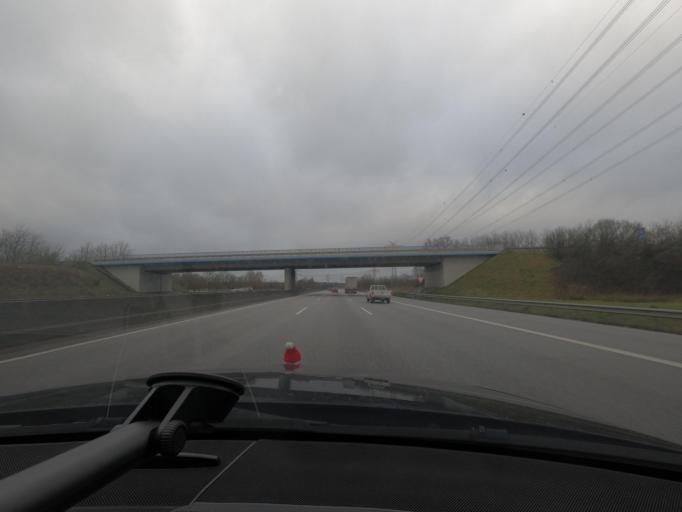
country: DE
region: Schleswig-Holstein
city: Alveslohe
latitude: 53.8035
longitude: 9.9291
